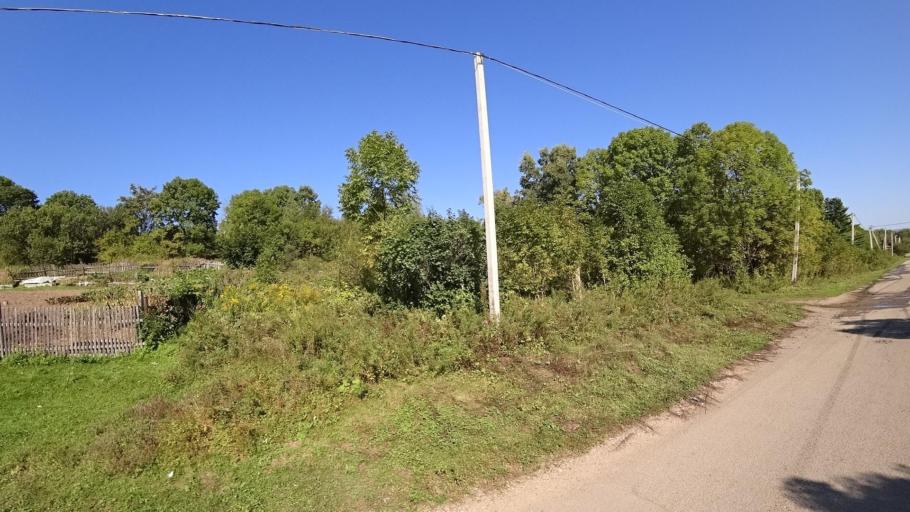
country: RU
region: Jewish Autonomous Oblast
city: Bira
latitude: 49.0090
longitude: 132.4726
